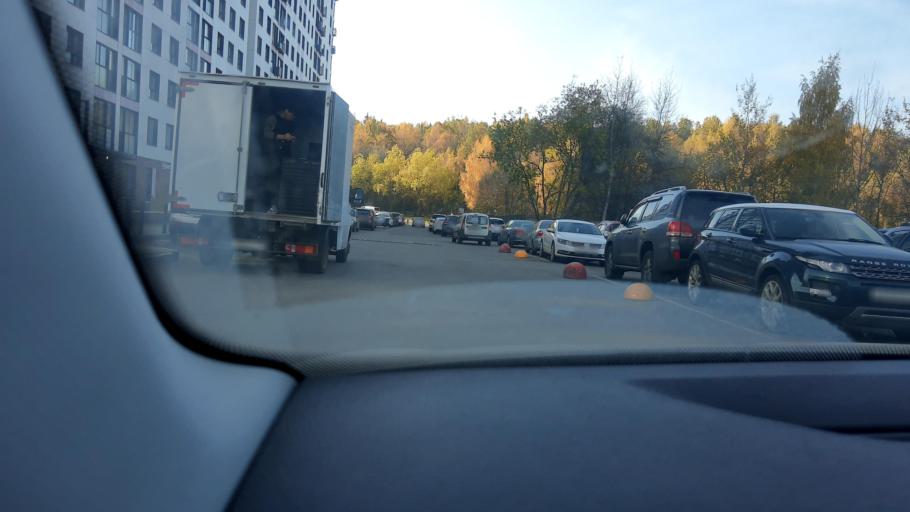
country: RU
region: Moscow
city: Annino
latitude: 55.5605
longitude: 37.5759
